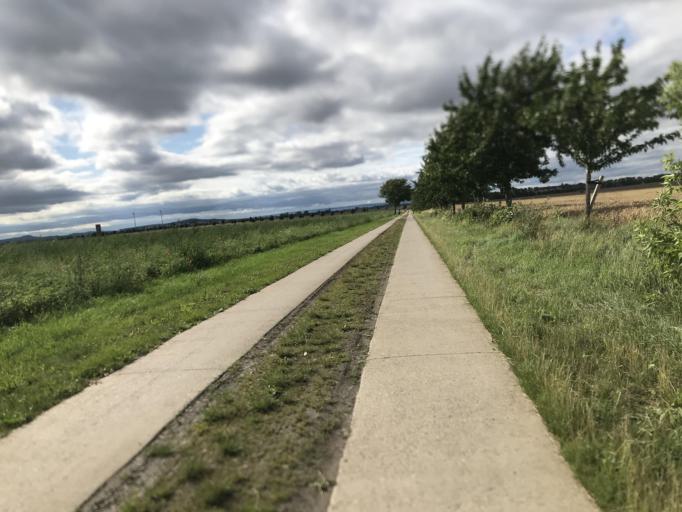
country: DE
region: Saxony-Anhalt
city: Gatersleben
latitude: 51.8042
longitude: 11.2471
